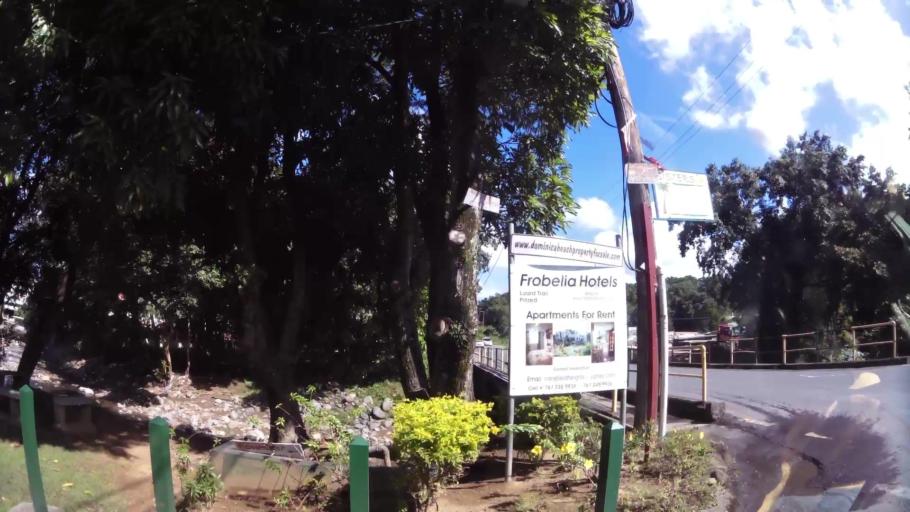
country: DM
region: Saint John
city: Portsmouth
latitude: 15.5591
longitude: -61.4566
